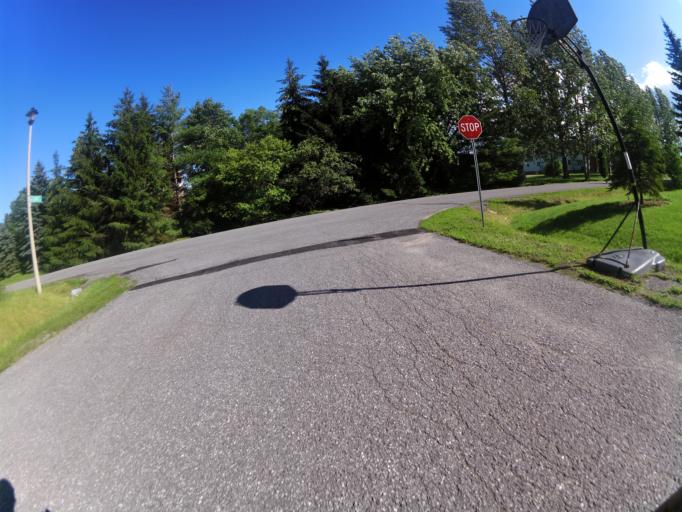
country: CA
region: Ontario
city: Bells Corners
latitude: 45.2634
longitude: -75.8226
